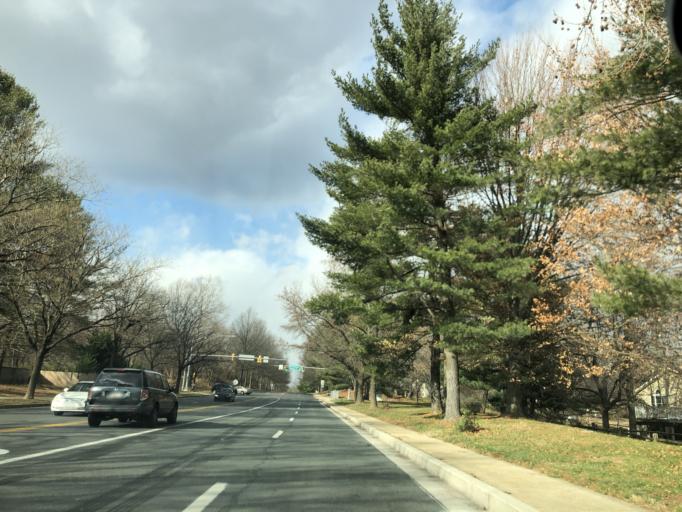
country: US
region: Maryland
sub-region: Howard County
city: Columbia
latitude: 39.1902
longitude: -76.8307
